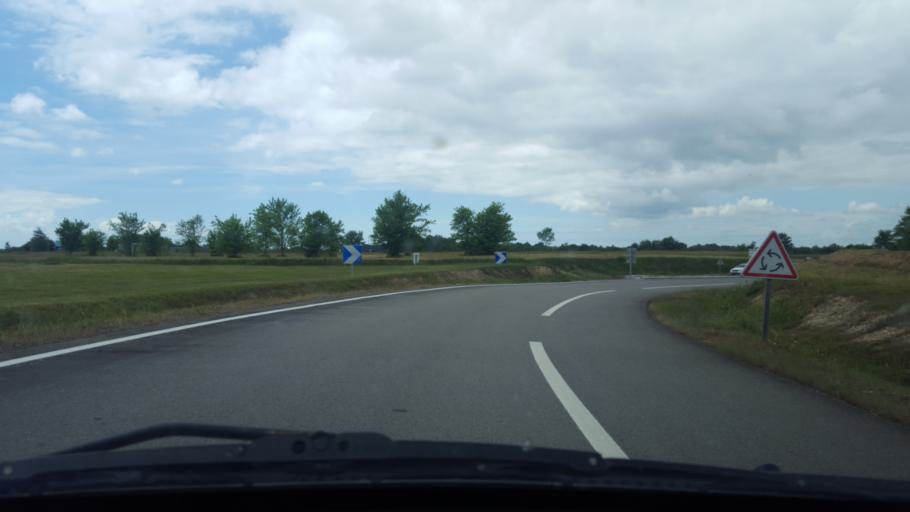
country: FR
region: Pays de la Loire
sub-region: Departement de la Loire-Atlantique
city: Paulx
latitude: 46.9998
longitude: -1.7354
